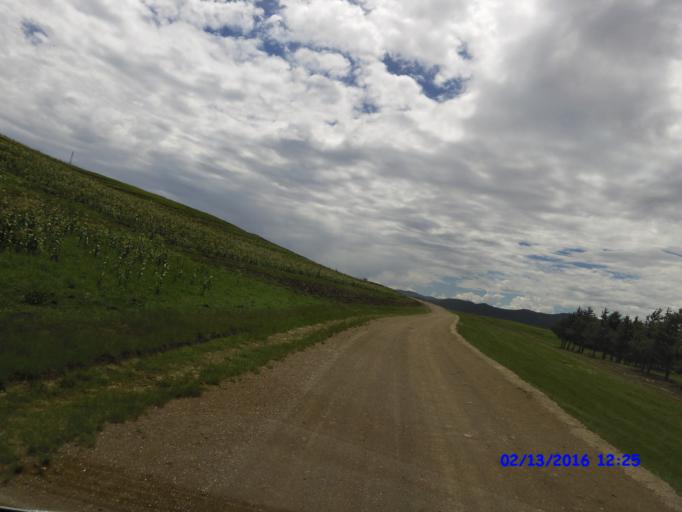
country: LS
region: Maseru
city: Nako
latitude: -29.8764
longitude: 28.0428
